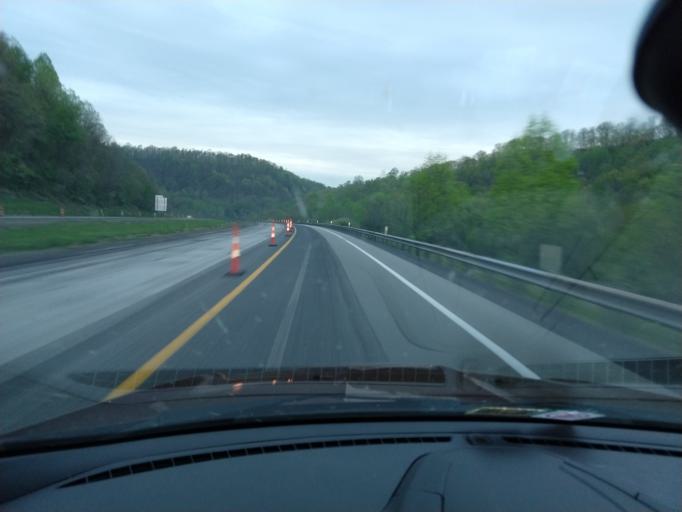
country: US
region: West Virginia
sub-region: Braxton County
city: Sutton
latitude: 38.7223
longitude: -80.6647
